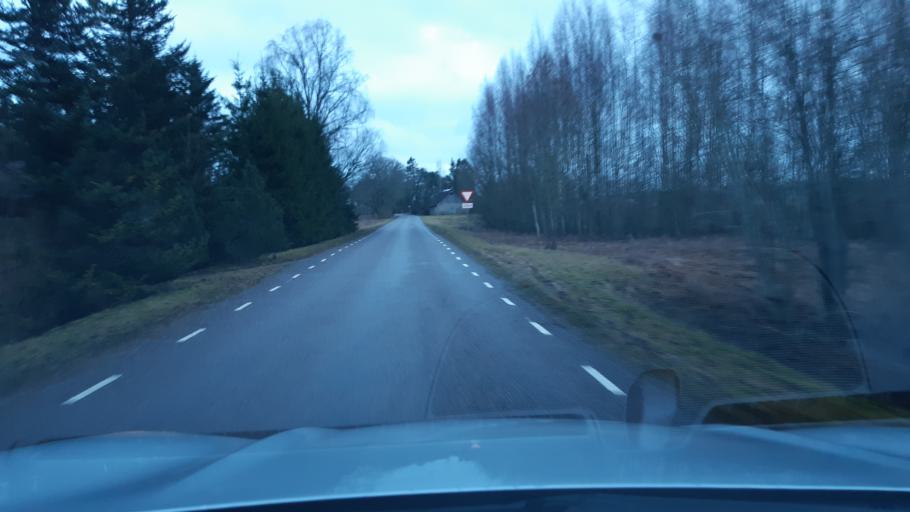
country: EE
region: Raplamaa
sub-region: Rapla vald
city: Rapla
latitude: 58.9831
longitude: 24.7350
